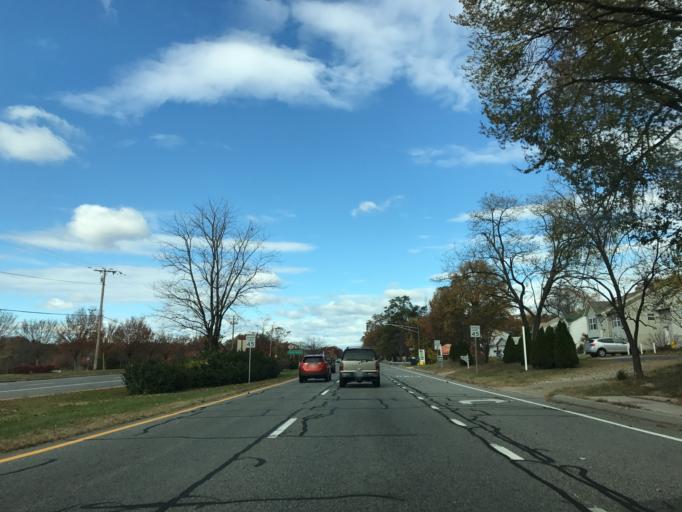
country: US
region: Maryland
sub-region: Anne Arundel County
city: South Gate
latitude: 39.1410
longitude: -76.6030
